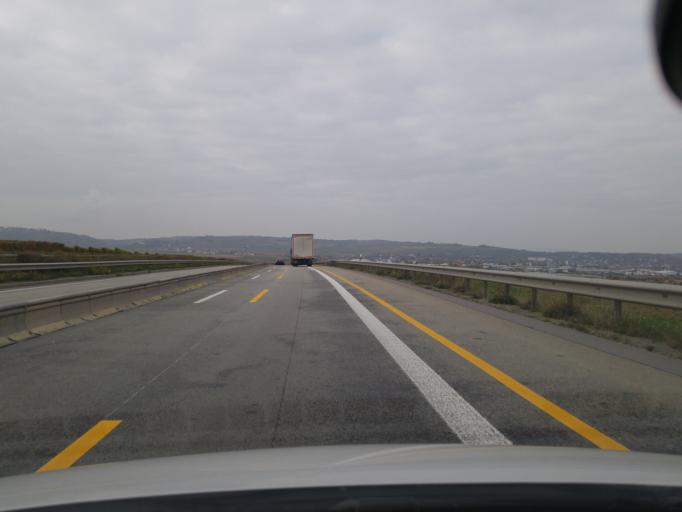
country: DE
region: Rheinland-Pfalz
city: Bissersheim
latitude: 49.5513
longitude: 8.2076
